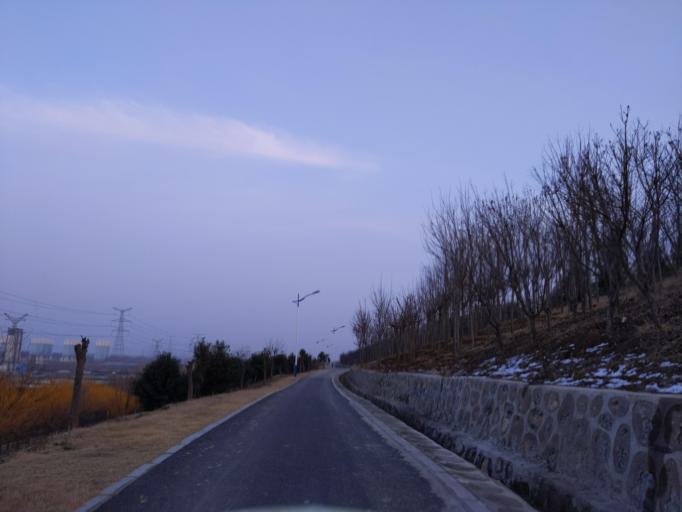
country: CN
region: Henan Sheng
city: Zhongyuanlu
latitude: 35.8170
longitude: 115.0550
